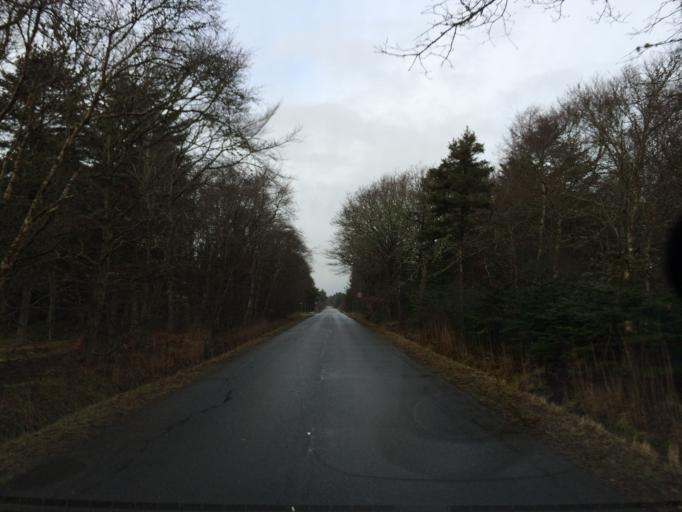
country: DK
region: Central Jutland
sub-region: Holstebro Kommune
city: Ulfborg
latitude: 56.2638
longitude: 8.1511
